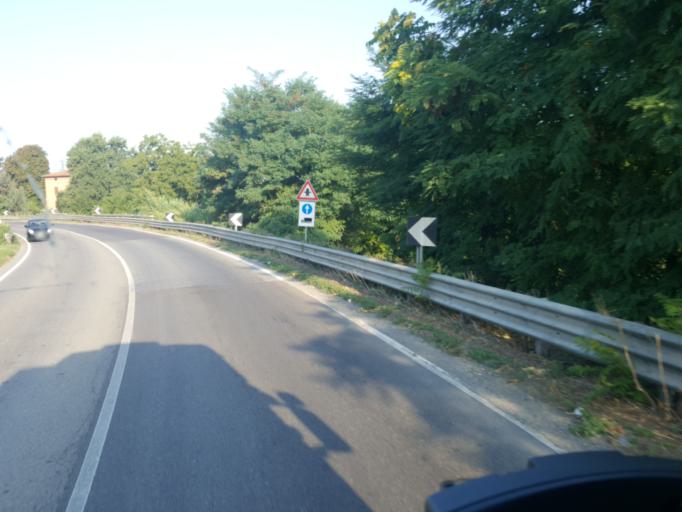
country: IT
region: Emilia-Romagna
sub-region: Provincia di Modena
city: Spilamberto
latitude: 44.5372
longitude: 10.9977
